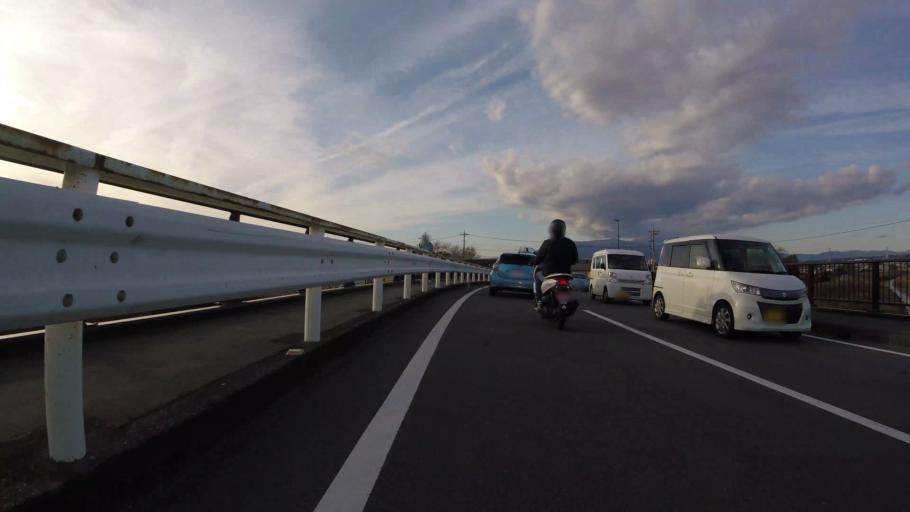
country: JP
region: Shizuoka
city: Mishima
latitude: 35.0924
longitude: 138.9348
